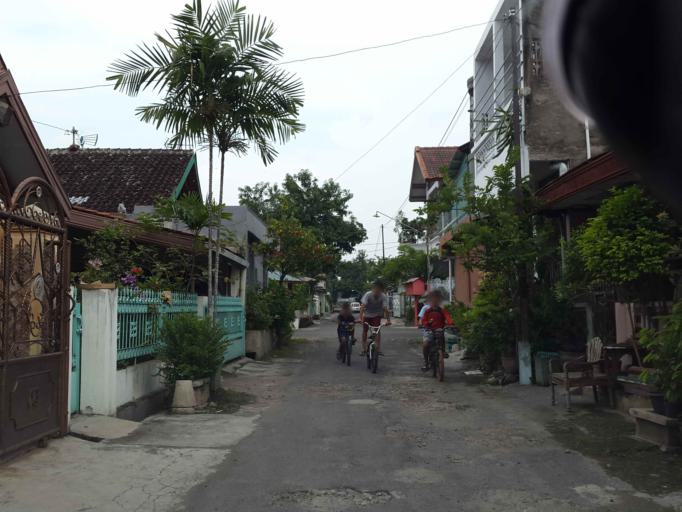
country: ID
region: Central Java
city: Surakarta
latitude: -7.5487
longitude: 110.8055
